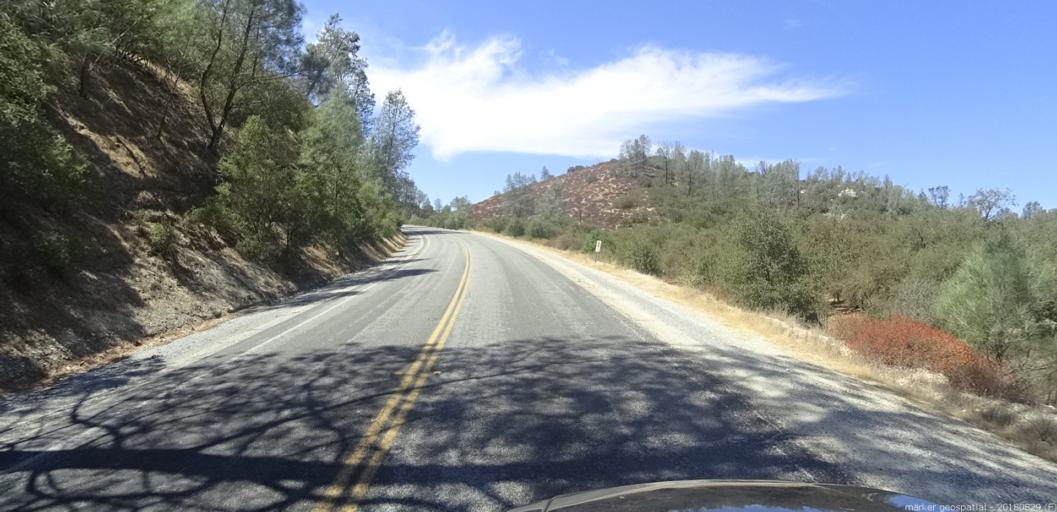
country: US
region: California
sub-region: San Luis Obispo County
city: Lake Nacimiento
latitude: 35.9036
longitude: -120.9649
